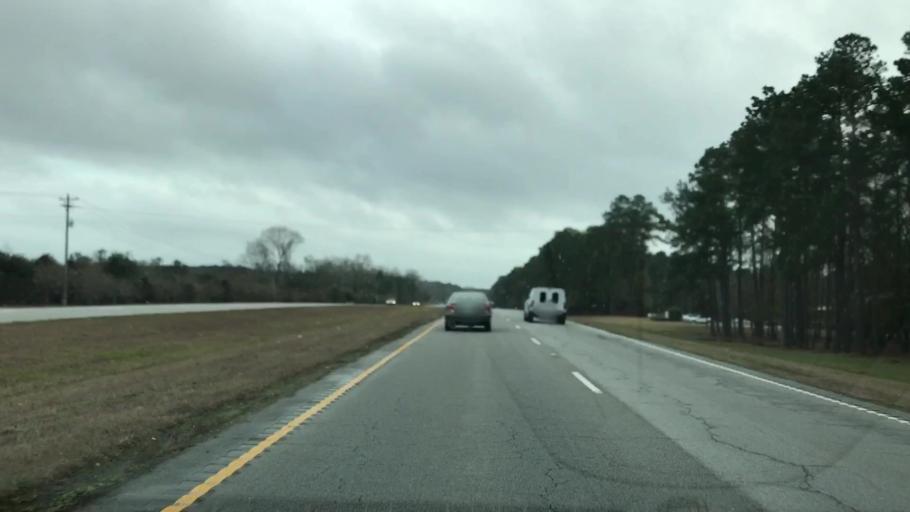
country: US
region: South Carolina
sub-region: Berkeley County
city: Moncks Corner
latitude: 33.1347
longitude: -80.0315
